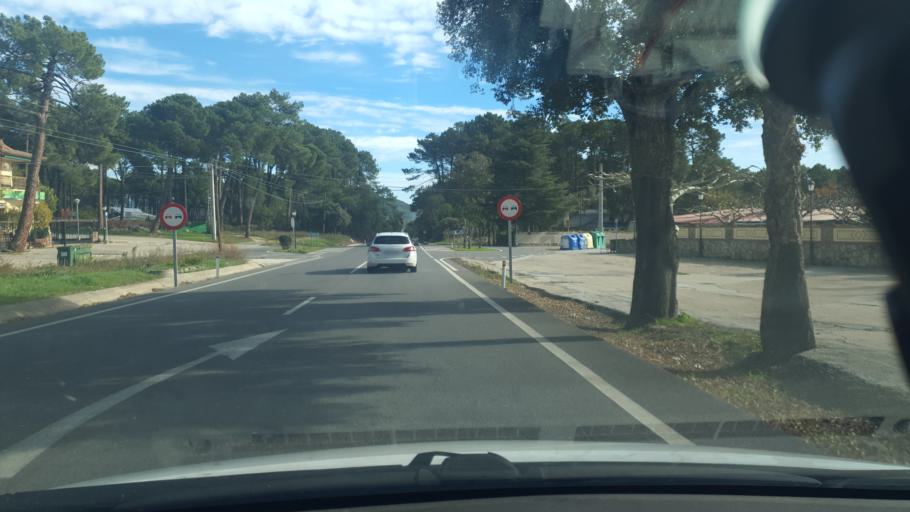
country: ES
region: Castille and Leon
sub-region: Provincia de Avila
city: La Adrada
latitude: 40.3102
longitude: -4.6565
